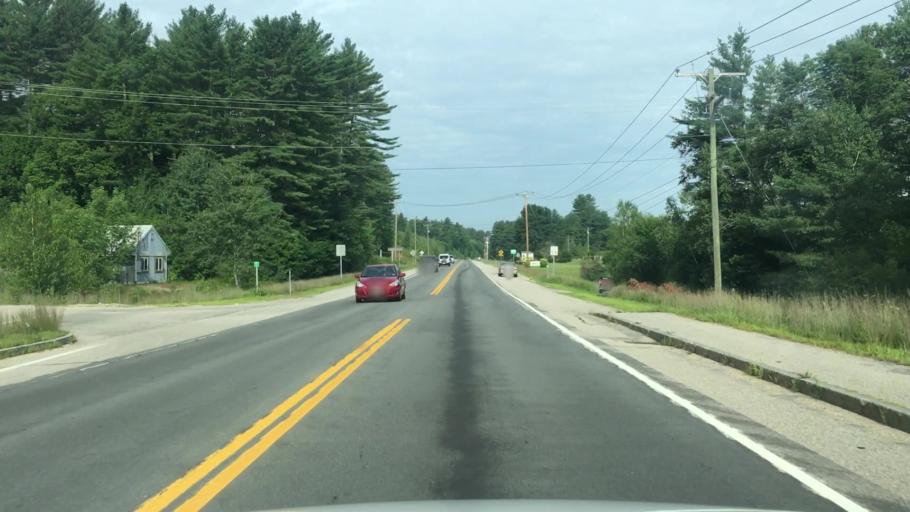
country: US
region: New Hampshire
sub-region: Carroll County
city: Tamworth
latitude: 43.8195
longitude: -71.2090
